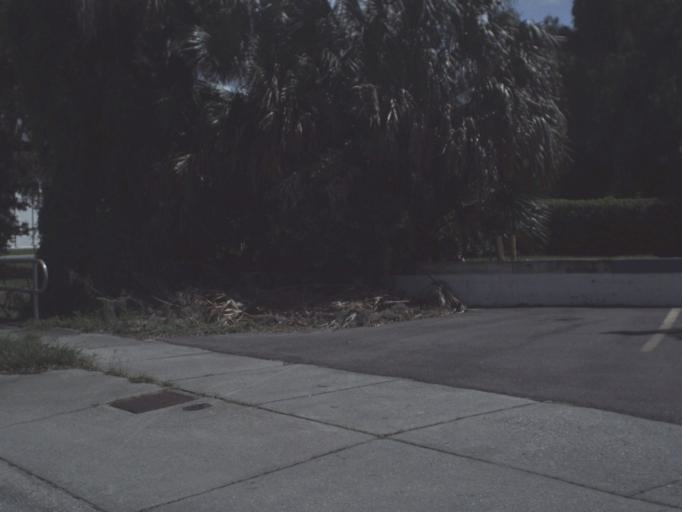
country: US
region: Florida
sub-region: Hillsborough County
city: Plant City
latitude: 28.0161
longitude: -82.1372
